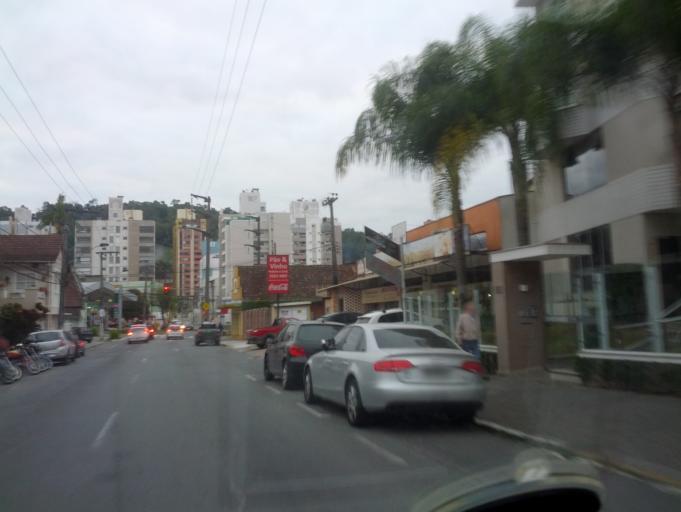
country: BR
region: Santa Catarina
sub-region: Blumenau
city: Blumenau
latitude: -26.9023
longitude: -49.0882
